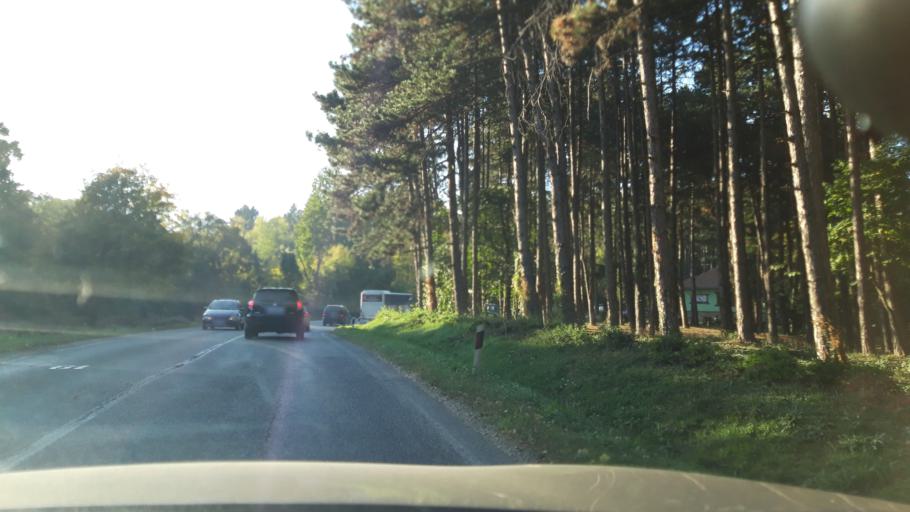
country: RS
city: Vrdnik
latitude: 45.1467
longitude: 19.8314
